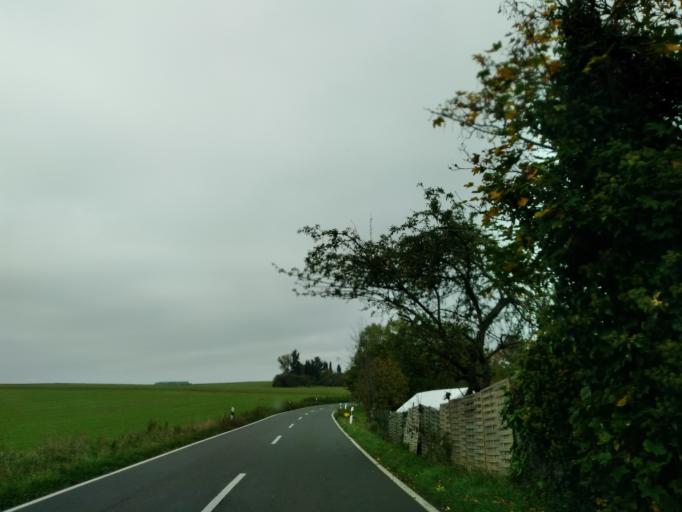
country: DE
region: North Rhine-Westphalia
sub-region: Regierungsbezirk Koln
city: Konigswinter
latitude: 50.7133
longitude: 7.2007
